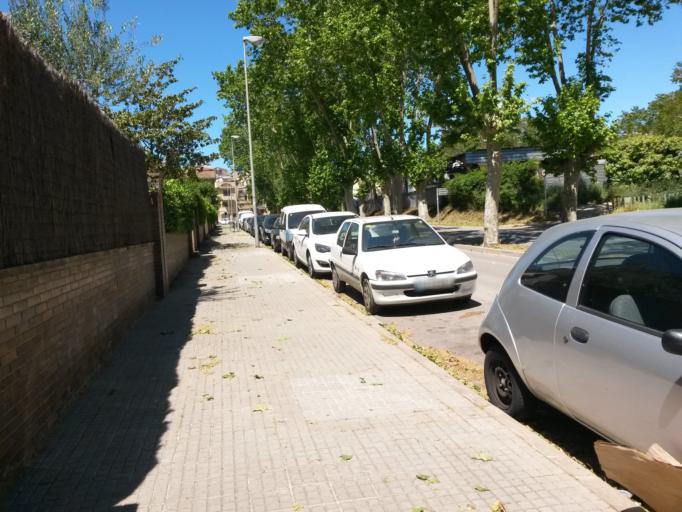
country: ES
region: Catalonia
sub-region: Provincia de Barcelona
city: Cerdanyola del Valles
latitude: 41.4874
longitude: 2.1321
